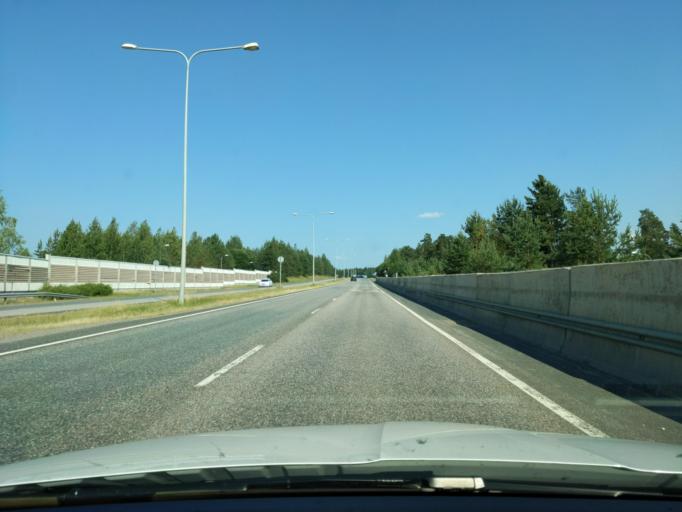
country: FI
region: Paijanne Tavastia
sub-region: Lahti
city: Hollola
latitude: 60.9868
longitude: 25.5235
